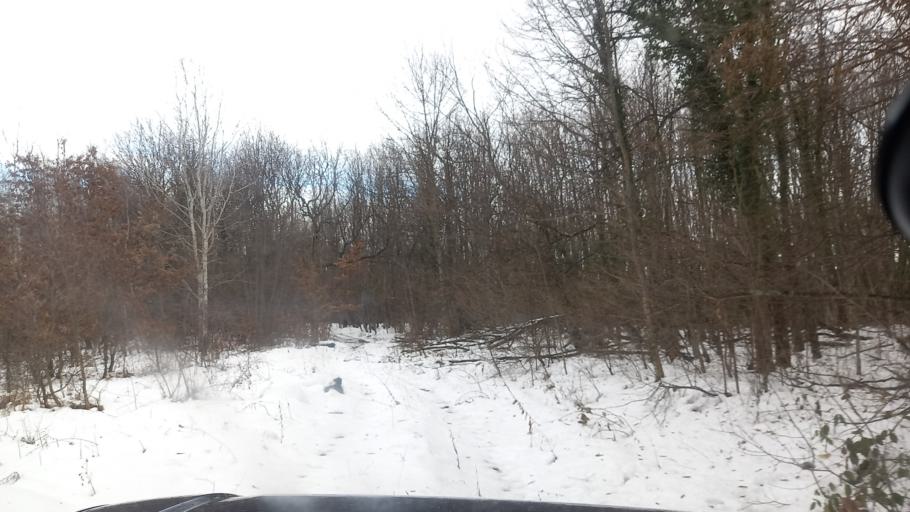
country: RU
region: Adygeya
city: Kamennomostskiy
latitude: 44.2554
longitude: 40.1835
